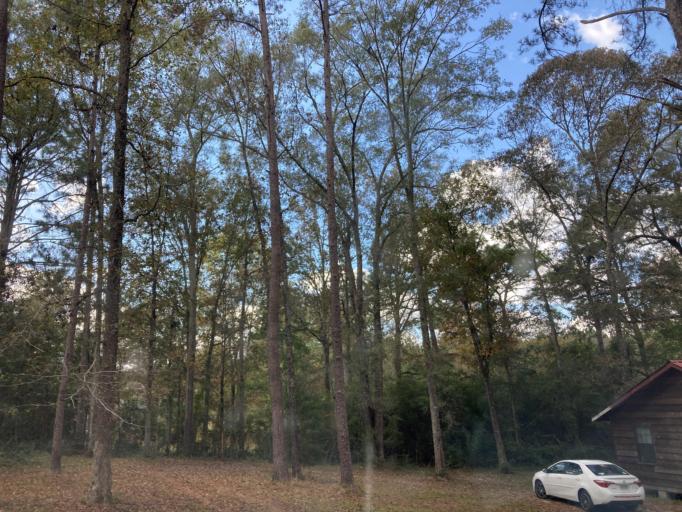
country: US
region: Mississippi
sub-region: Lamar County
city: Sumrall
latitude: 31.3751
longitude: -89.5437
